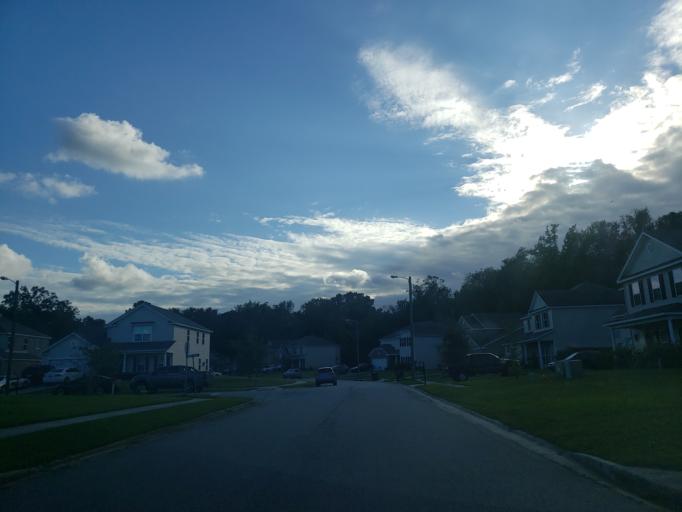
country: US
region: Georgia
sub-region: Chatham County
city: Georgetown
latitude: 31.9967
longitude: -81.2444
